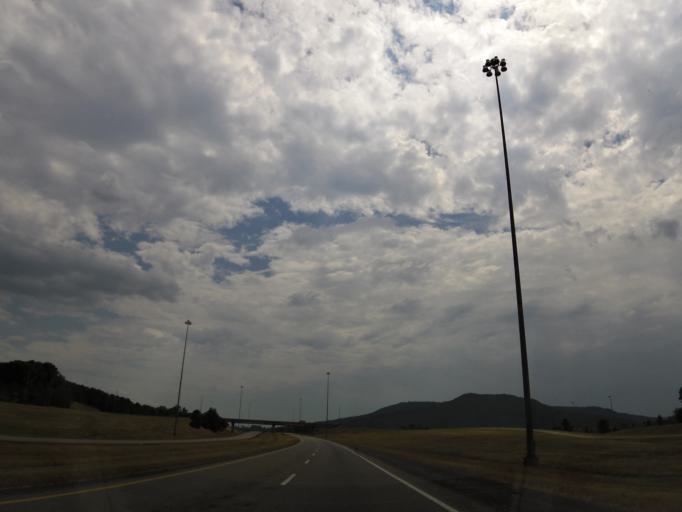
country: US
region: Alabama
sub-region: Jackson County
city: Bridgeport
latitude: 34.9789
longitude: -85.7333
